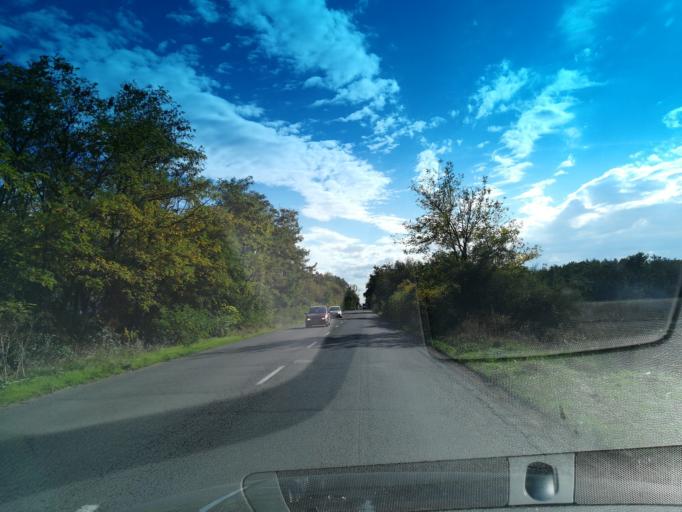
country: BG
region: Stara Zagora
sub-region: Obshtina Stara Zagora
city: Stara Zagora
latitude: 42.3550
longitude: 25.6575
